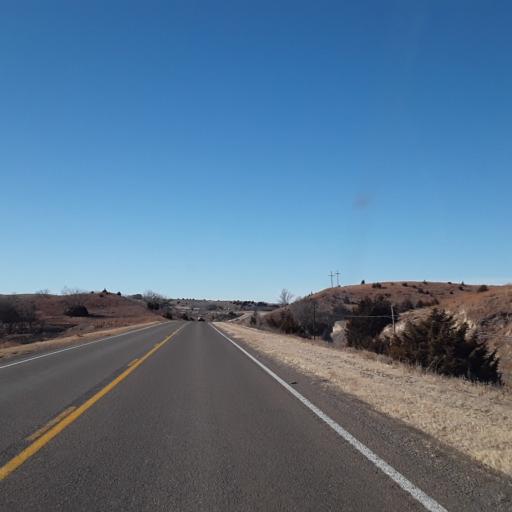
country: US
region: Nebraska
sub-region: Frontier County
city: Stockville
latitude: 40.6309
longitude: -100.5610
